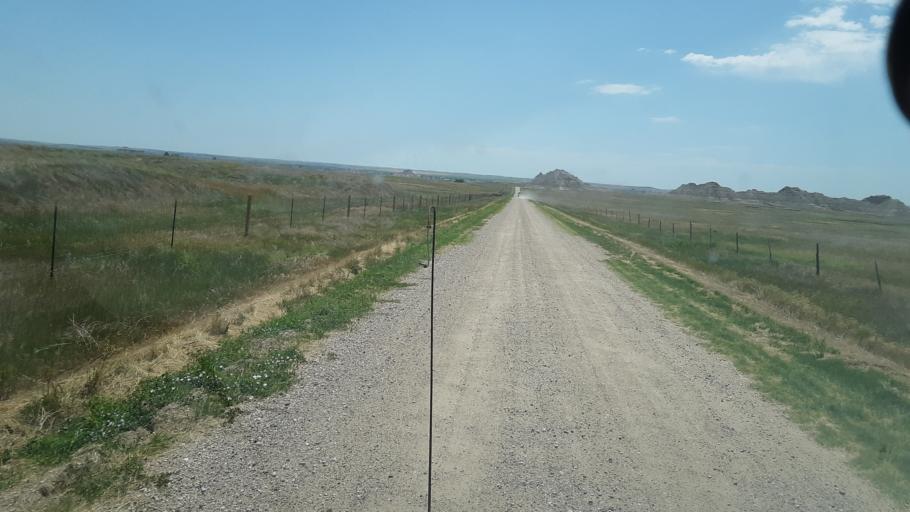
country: US
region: South Dakota
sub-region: Haakon County
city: Philip
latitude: 43.7463
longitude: -101.9995
